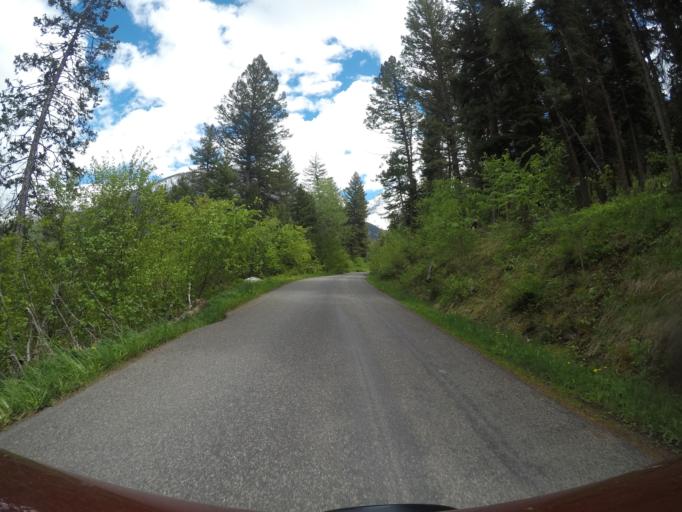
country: US
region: Montana
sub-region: Park County
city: Livingston
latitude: 45.4987
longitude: -110.5325
